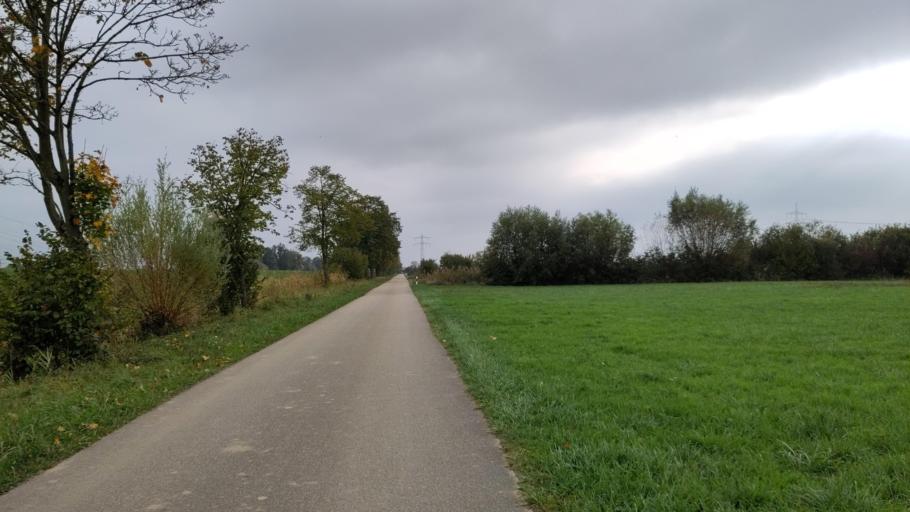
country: DE
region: Baden-Wuerttemberg
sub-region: Freiburg Region
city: Riegel
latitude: 48.1379
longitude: 7.7562
